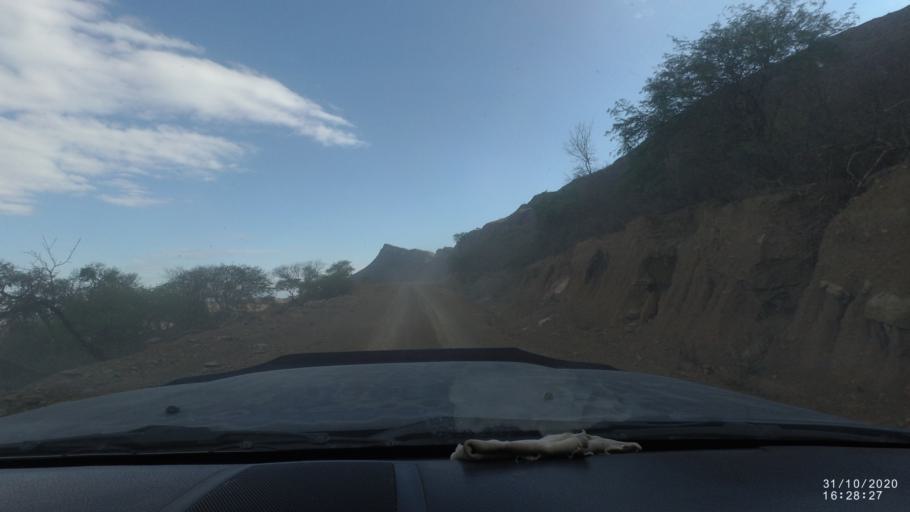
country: BO
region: Chuquisaca
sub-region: Provincia Zudanez
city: Mojocoya
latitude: -18.4127
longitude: -64.5866
